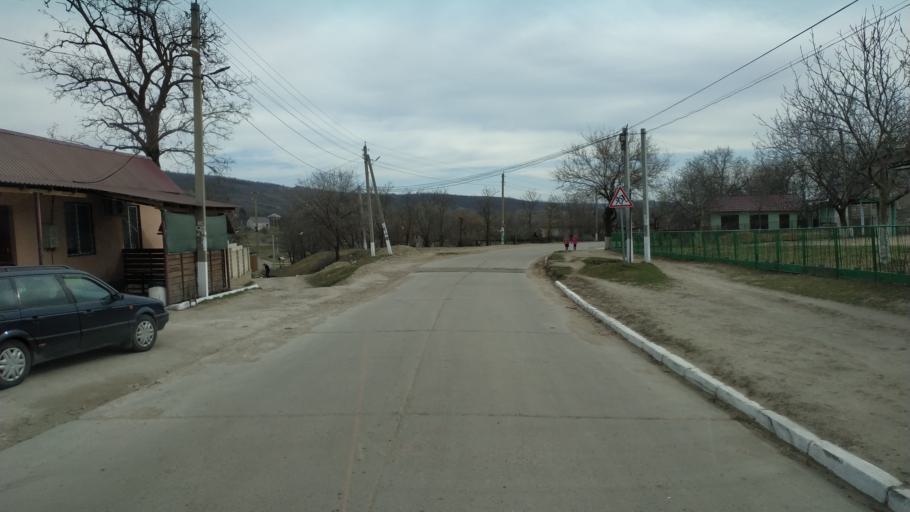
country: MD
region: Hincesti
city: Dancu
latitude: 46.9225
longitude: 28.2678
